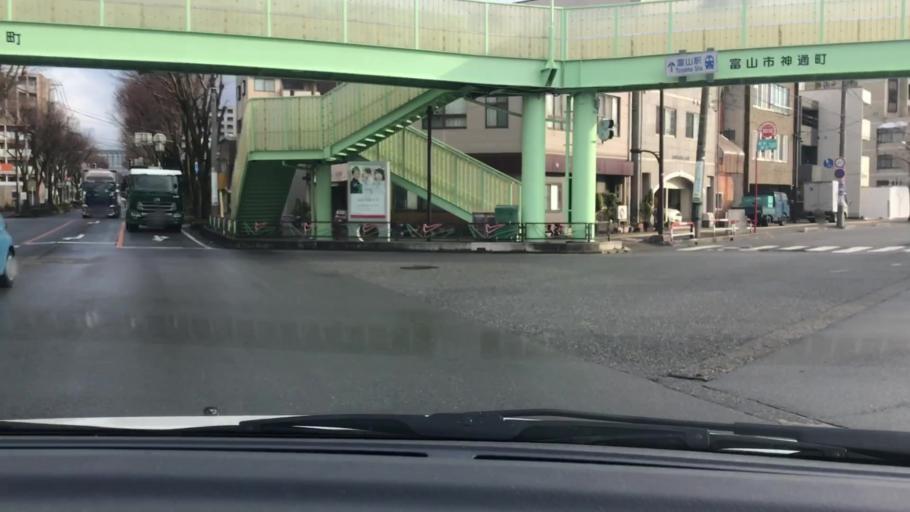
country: JP
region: Toyama
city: Toyama-shi
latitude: 36.7002
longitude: 137.2066
